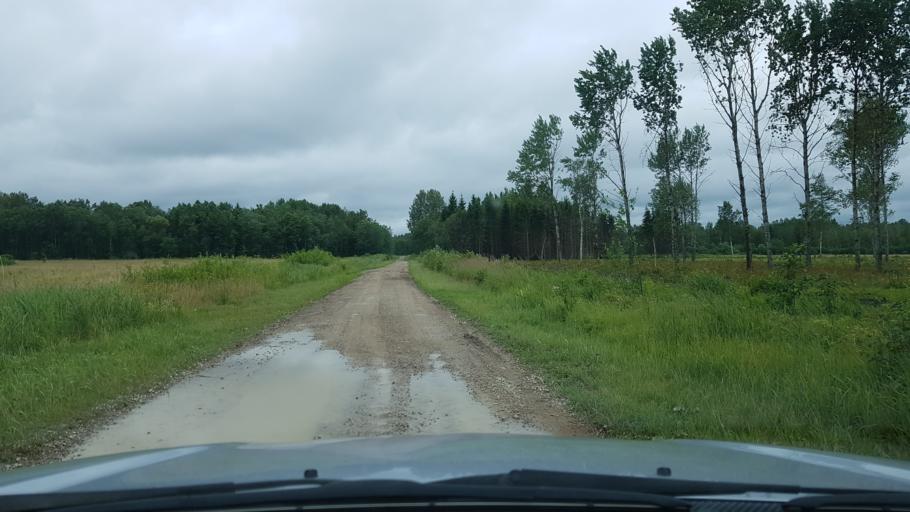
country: EE
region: Ida-Virumaa
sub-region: Narva-Joesuu linn
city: Narva-Joesuu
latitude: 59.3673
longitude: 27.9257
